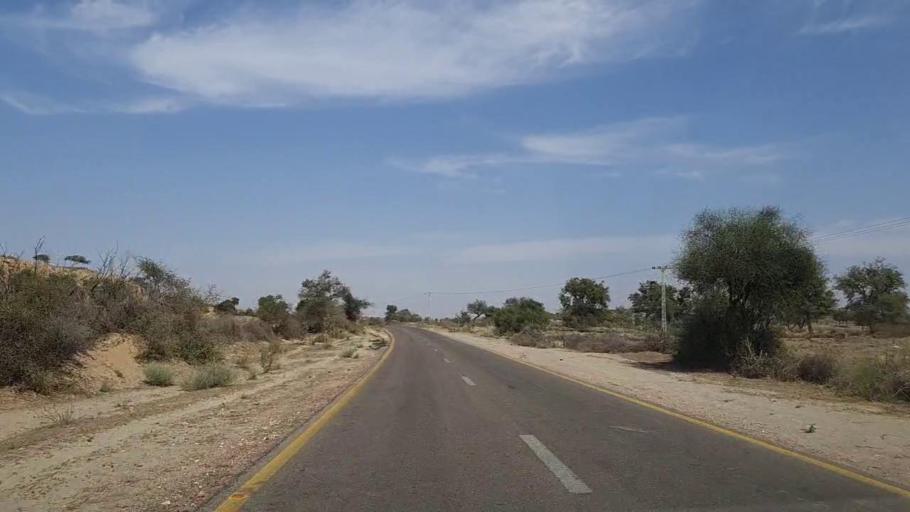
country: PK
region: Sindh
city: Mithi
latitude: 24.7931
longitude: 69.8145
